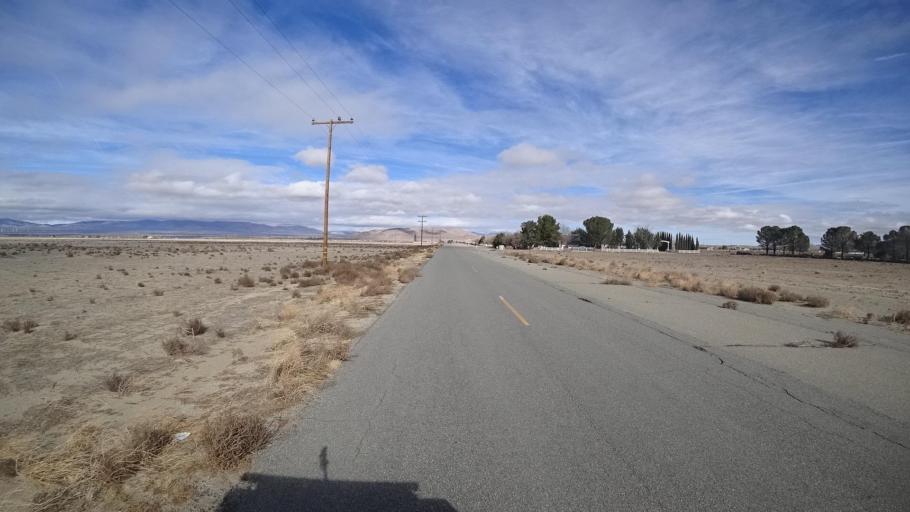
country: US
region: California
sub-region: Kern County
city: Rosamond
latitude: 34.8281
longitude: -118.2730
